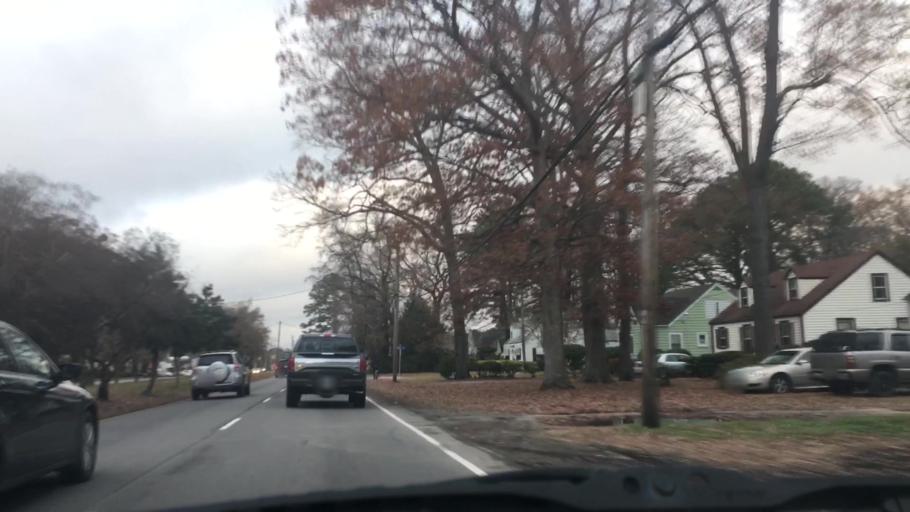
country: US
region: Virginia
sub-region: City of Norfolk
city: Norfolk
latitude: 36.9267
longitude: -76.2432
